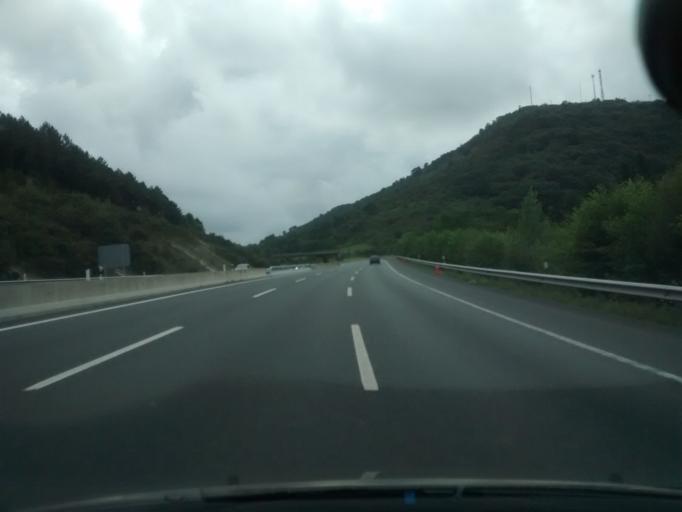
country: ES
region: Basque Country
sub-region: Provincia de Guipuzcoa
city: Usurbil
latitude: 43.2950
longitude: -2.0566
